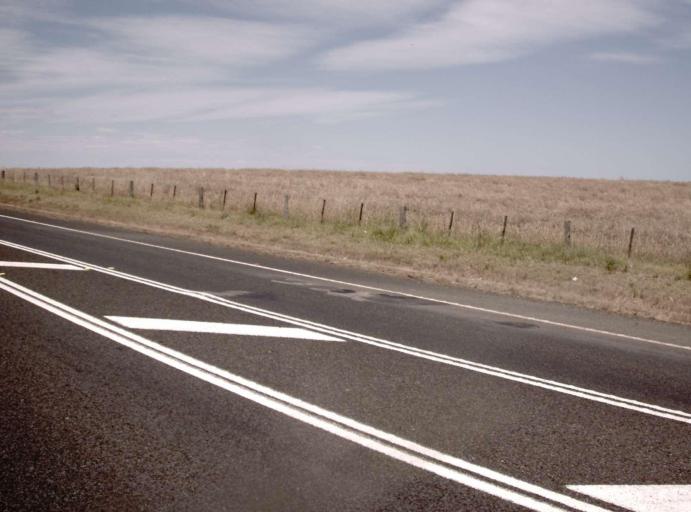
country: AU
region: Victoria
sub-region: Wellington
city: Heyfield
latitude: -38.1241
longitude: 146.8453
